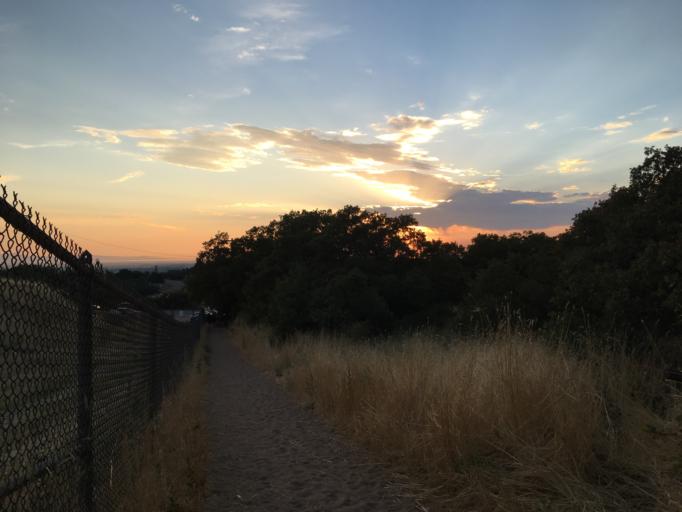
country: US
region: Utah
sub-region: Davis County
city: Fruit Heights
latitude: 41.0664
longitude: -111.9088
